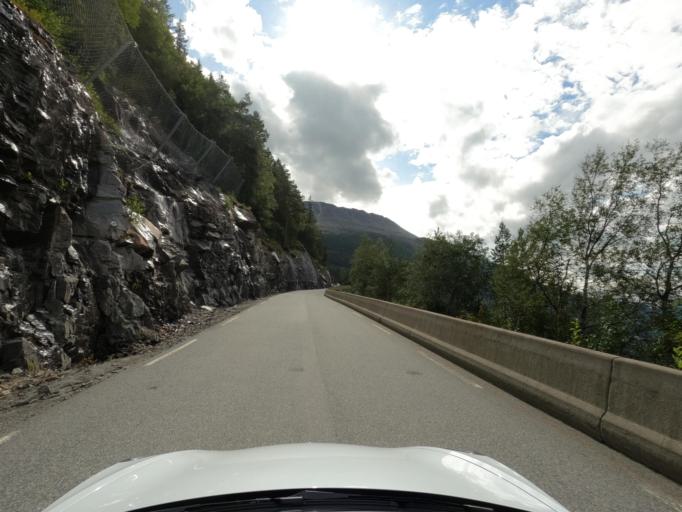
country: NO
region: Telemark
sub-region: Tinn
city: Rjukan
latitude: 59.8861
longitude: 8.6964
